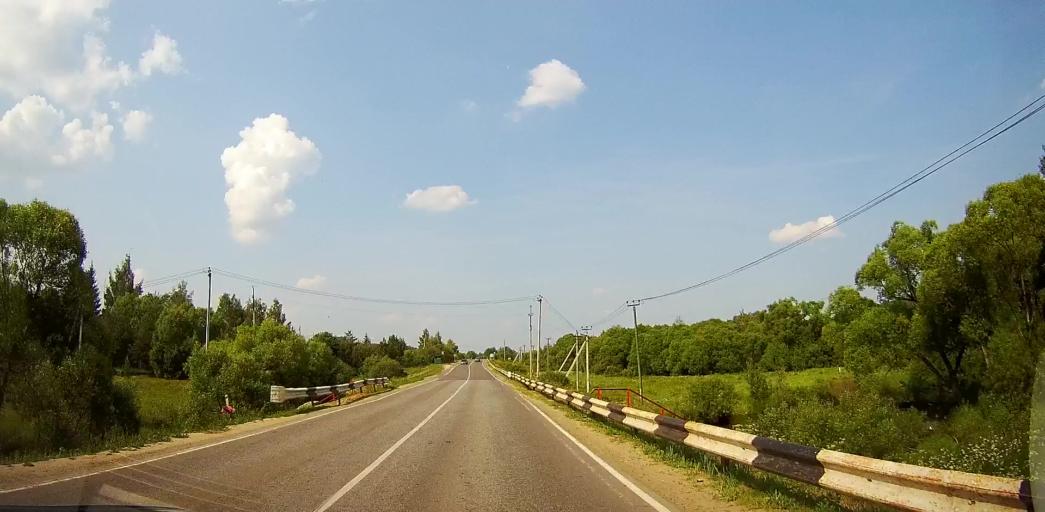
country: RU
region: Moskovskaya
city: Mikhnevo
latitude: 55.1819
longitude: 37.9741
